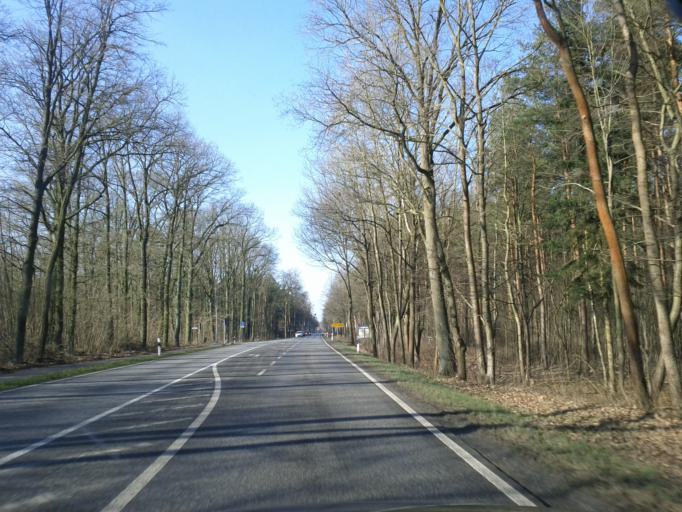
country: DE
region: Brandenburg
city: Spreenhagen
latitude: 52.4006
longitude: 13.9110
